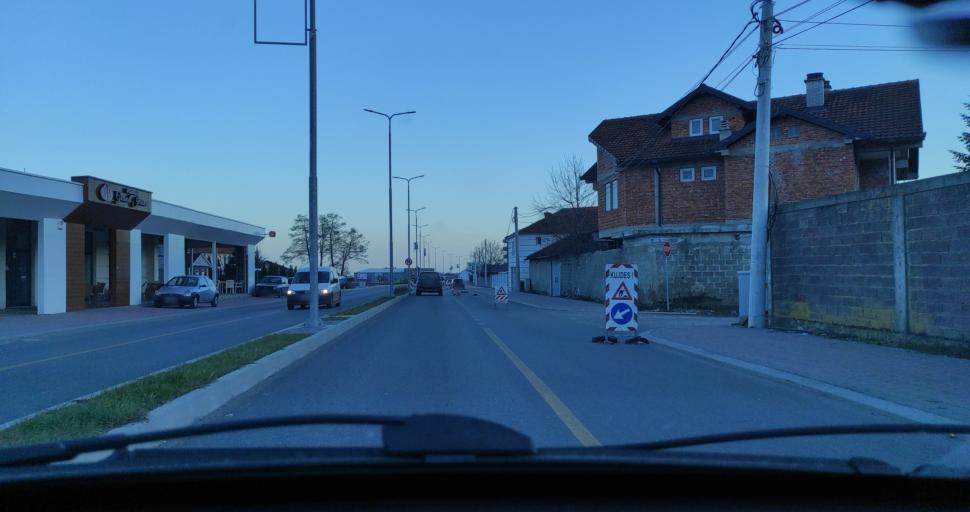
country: XK
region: Gjakova
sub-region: Komuna e Decanit
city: Dranoc
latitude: 42.5275
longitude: 20.2985
